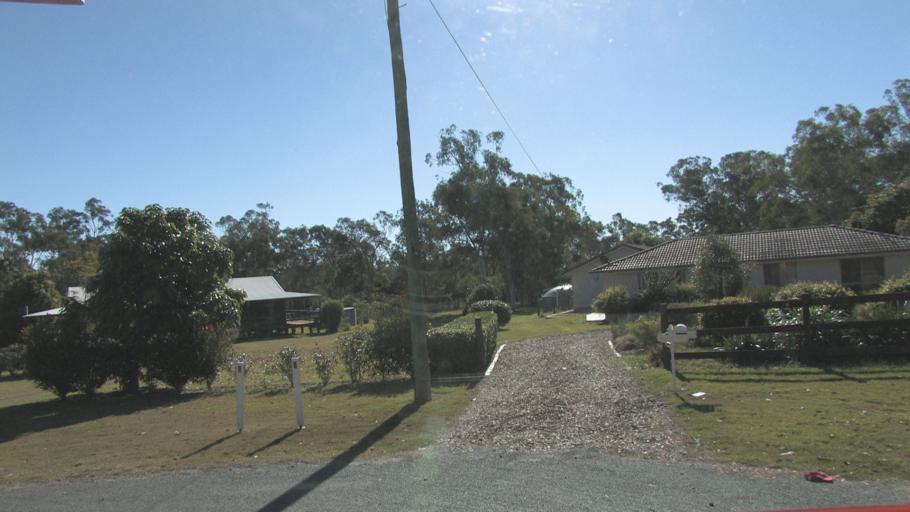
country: AU
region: Queensland
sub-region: Logan
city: Chambers Flat
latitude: -27.7362
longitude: 153.0642
